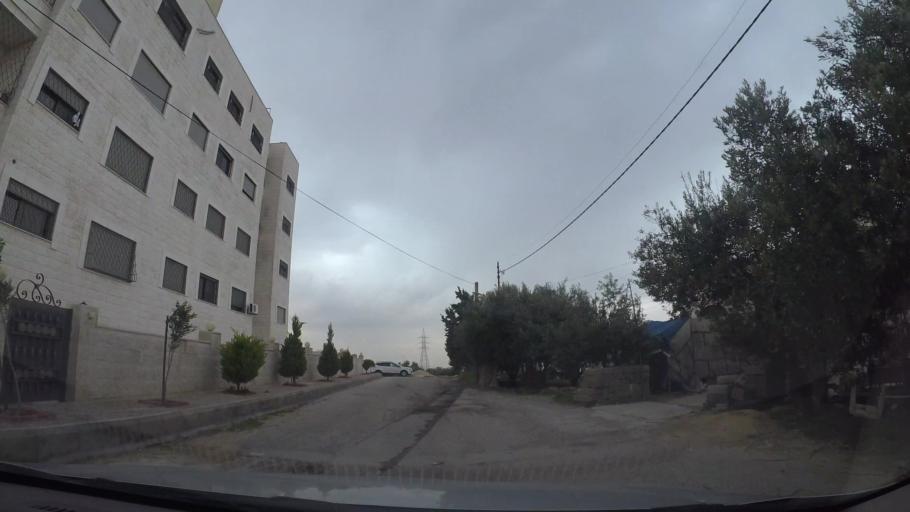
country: JO
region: Amman
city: Umm as Summaq
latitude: 31.9059
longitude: 35.8332
